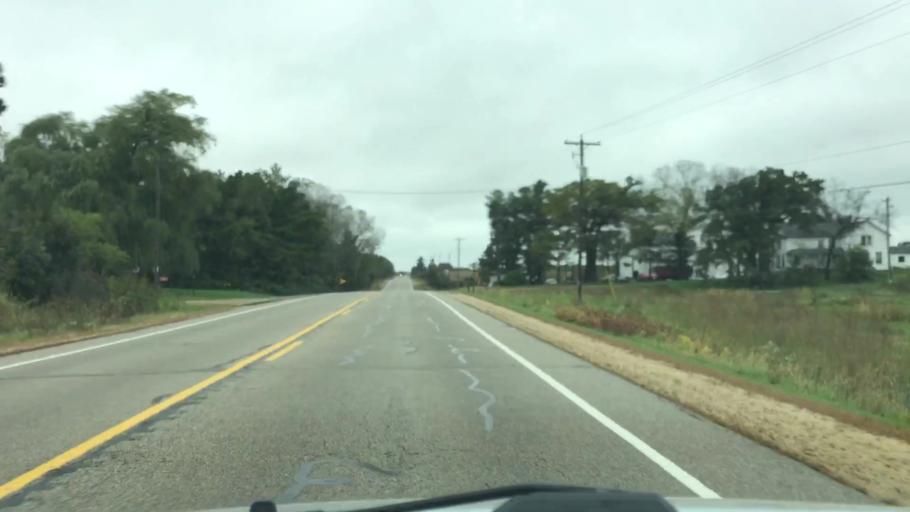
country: US
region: Wisconsin
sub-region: Rock County
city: Milton
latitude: 42.7720
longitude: -88.8840
